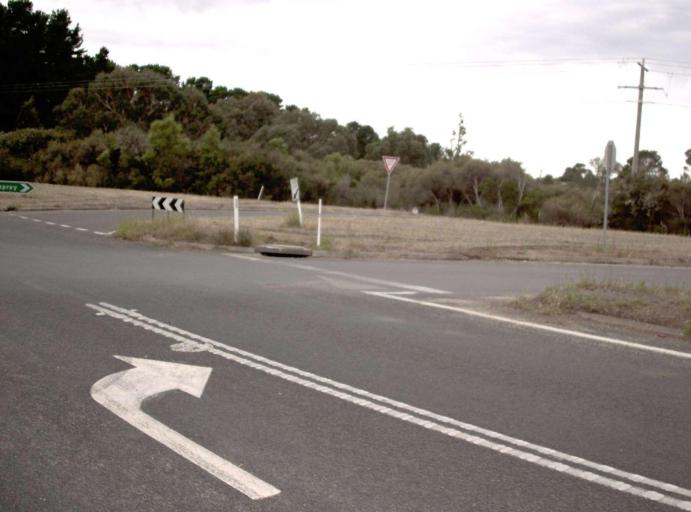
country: AU
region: Victoria
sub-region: Wellington
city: Sale
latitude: -38.1744
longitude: 147.0878
